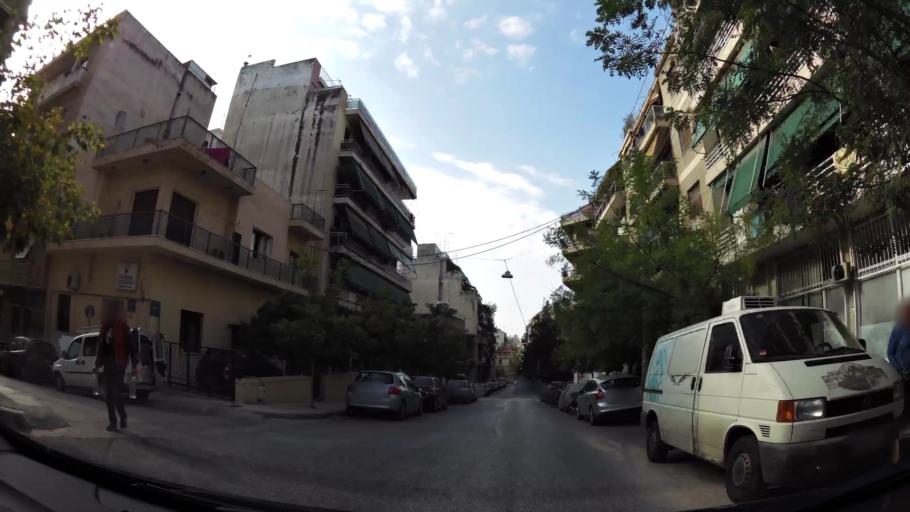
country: GR
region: Attica
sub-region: Nomarchia Athinas
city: Kipseli
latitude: 38.0062
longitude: 23.7445
